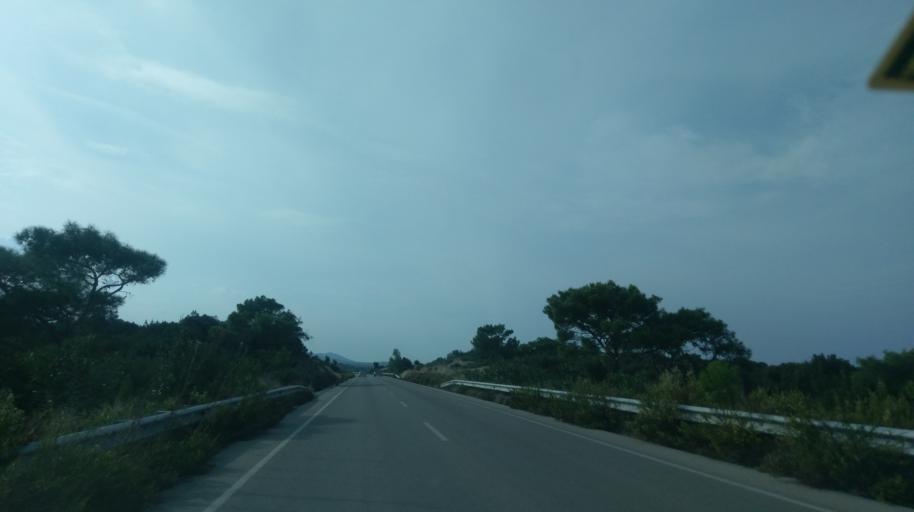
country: CY
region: Ammochostos
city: Trikomo
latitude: 35.4137
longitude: 33.8636
